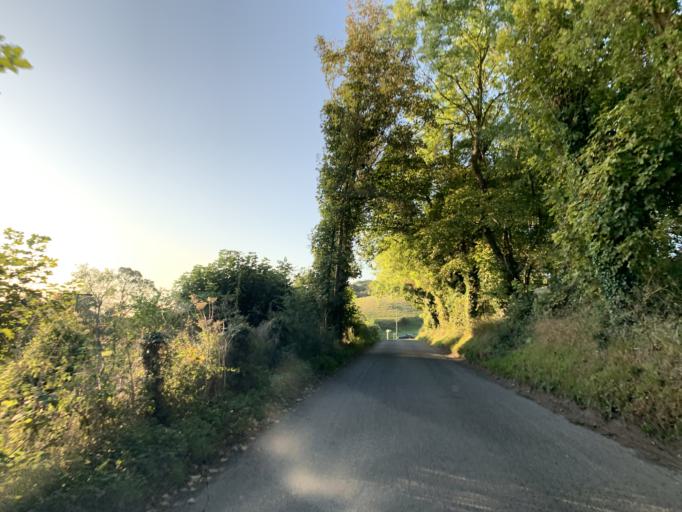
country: GB
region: England
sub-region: Wiltshire
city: Woodford
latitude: 51.1064
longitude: -1.8310
